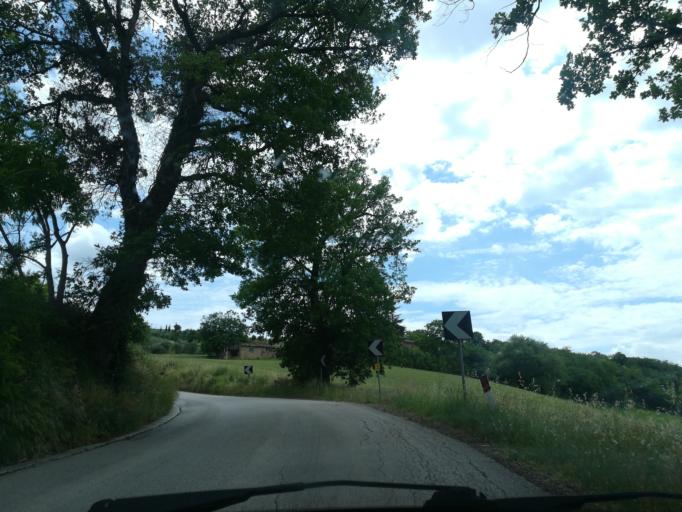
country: IT
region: The Marches
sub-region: Provincia di Macerata
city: Petriolo
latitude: 43.2298
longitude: 13.4628
